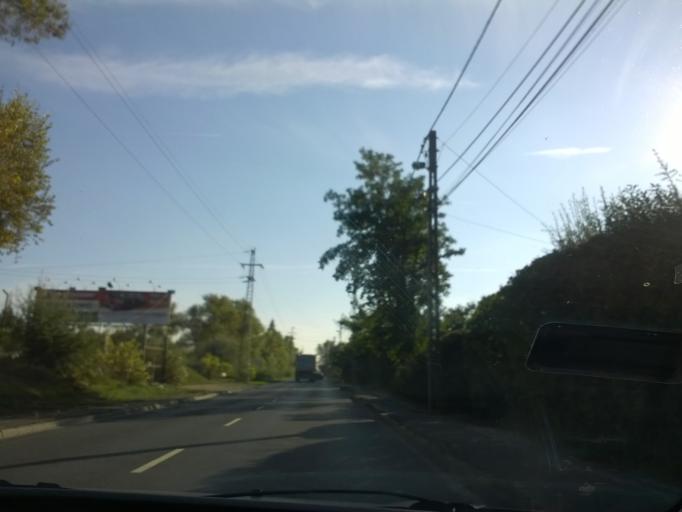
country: HU
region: Budapest
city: Budapest XXII. keruelet
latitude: 47.3939
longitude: 19.0539
